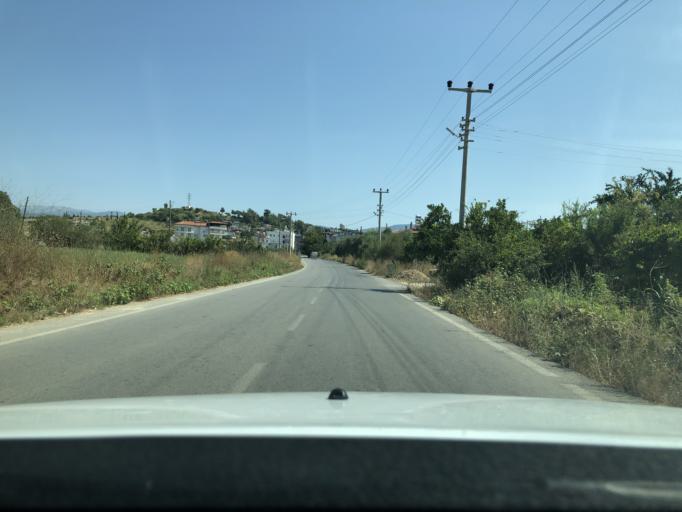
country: TR
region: Antalya
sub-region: Manavgat
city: Manavgat
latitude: 36.8077
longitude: 31.4804
